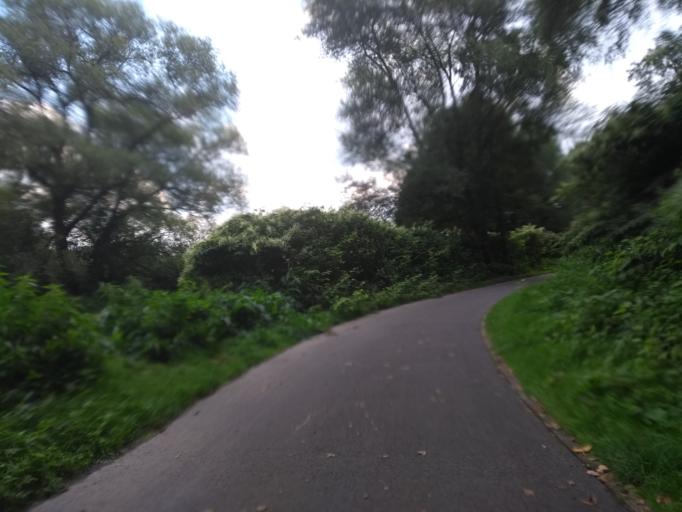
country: DE
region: North Rhine-Westphalia
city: Witten
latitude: 51.4017
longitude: 7.3493
